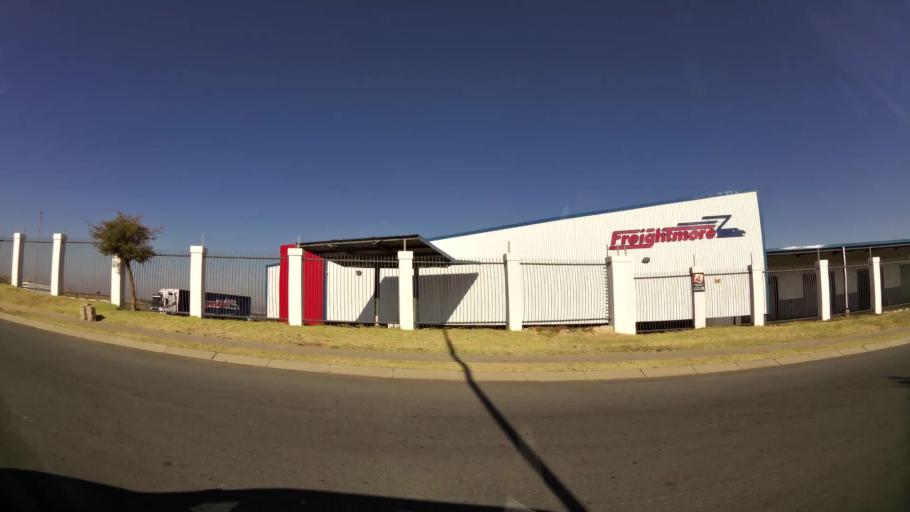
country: ZA
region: Gauteng
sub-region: City of Johannesburg Metropolitan Municipality
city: Modderfontein
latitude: -26.0551
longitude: 28.1665
